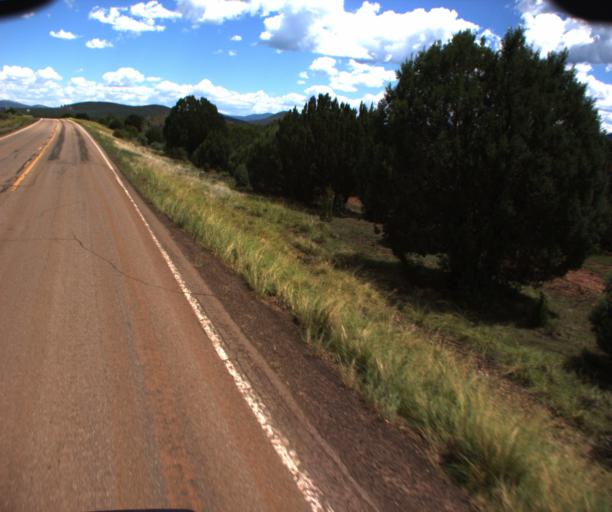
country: US
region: Arizona
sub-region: Navajo County
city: Pinetop-Lakeside
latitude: 34.2776
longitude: -109.7949
